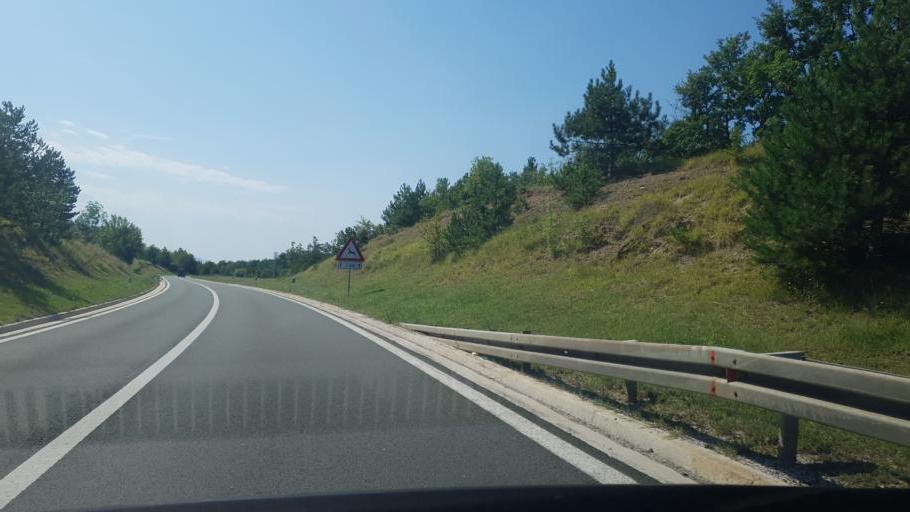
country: HR
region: Istarska
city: Buzet
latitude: 45.3283
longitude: 14.0741
